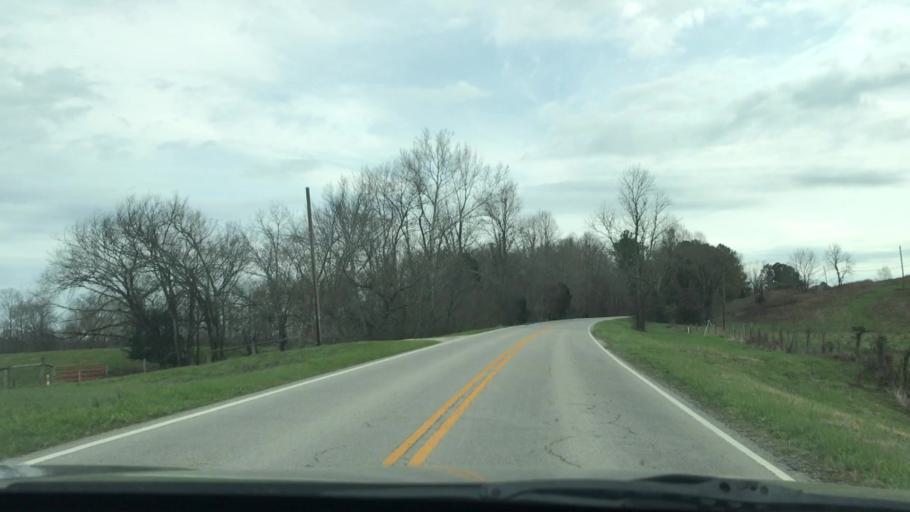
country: US
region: Kentucky
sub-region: Hart County
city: Munfordville
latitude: 37.3141
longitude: -85.7621
